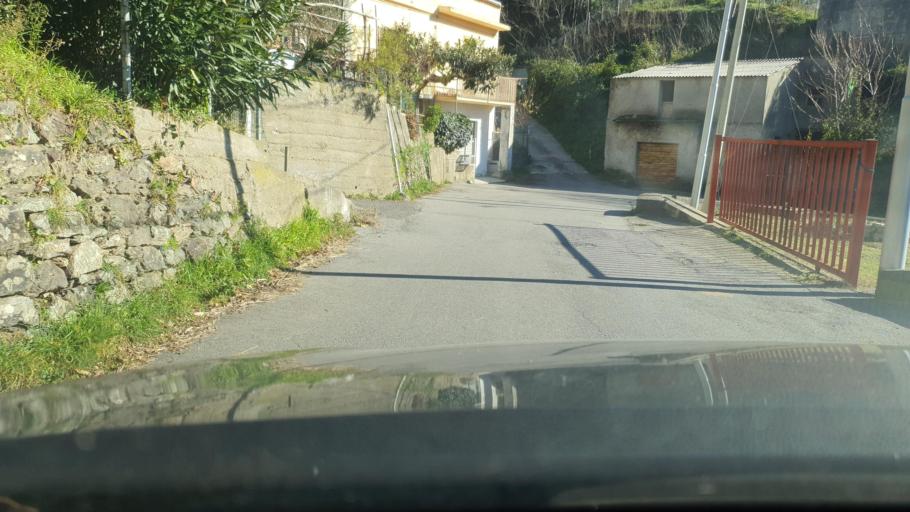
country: IT
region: Calabria
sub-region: Provincia di Catanzaro
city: Sant'Elia
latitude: 38.9579
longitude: 16.5796
